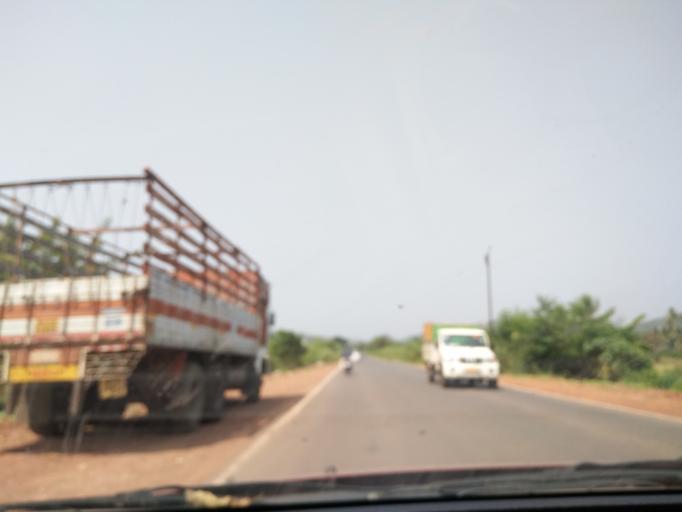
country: IN
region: Goa
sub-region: South Goa
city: Raia
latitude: 15.3010
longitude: 73.9701
